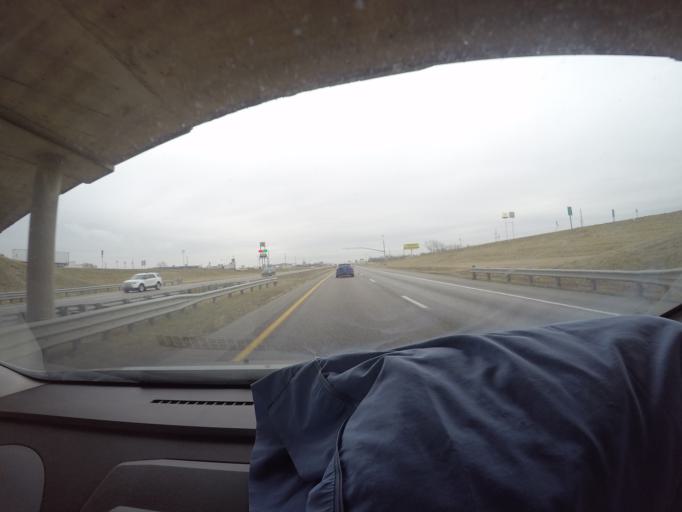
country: US
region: Missouri
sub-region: Warren County
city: Wright City
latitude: 38.8165
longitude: -90.9537
